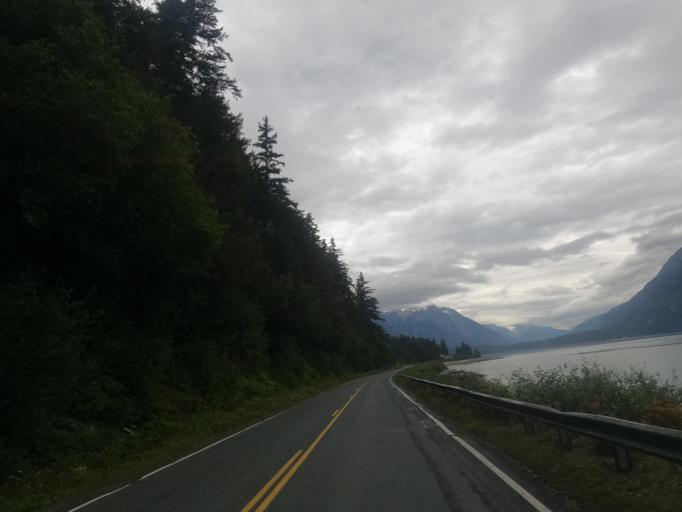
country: US
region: Alaska
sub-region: Haines Borough
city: Haines
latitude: 59.2936
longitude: -135.5032
